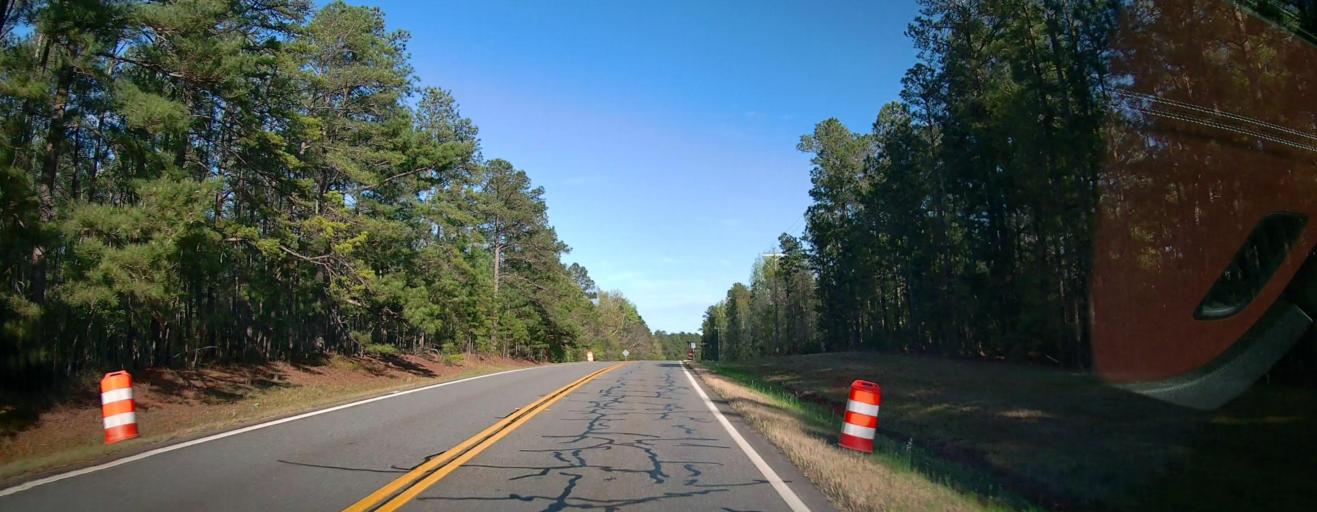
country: US
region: Georgia
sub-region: Baldwin County
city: Milledgeville
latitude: 33.1283
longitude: -83.3063
